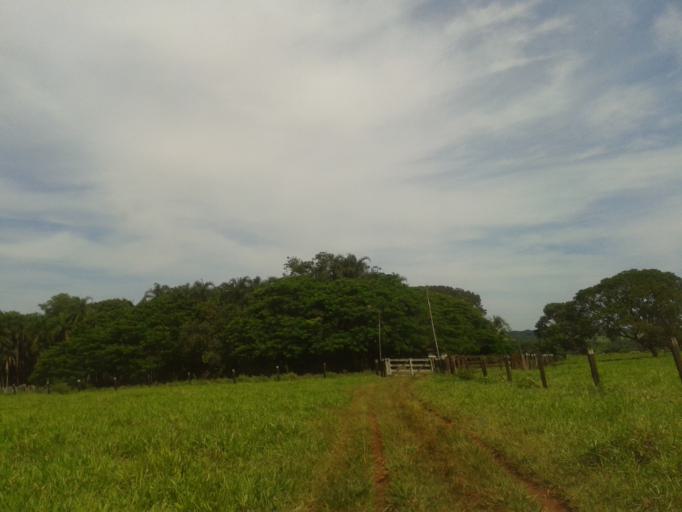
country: BR
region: Minas Gerais
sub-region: Santa Vitoria
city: Santa Vitoria
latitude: -19.1262
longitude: -50.5535
